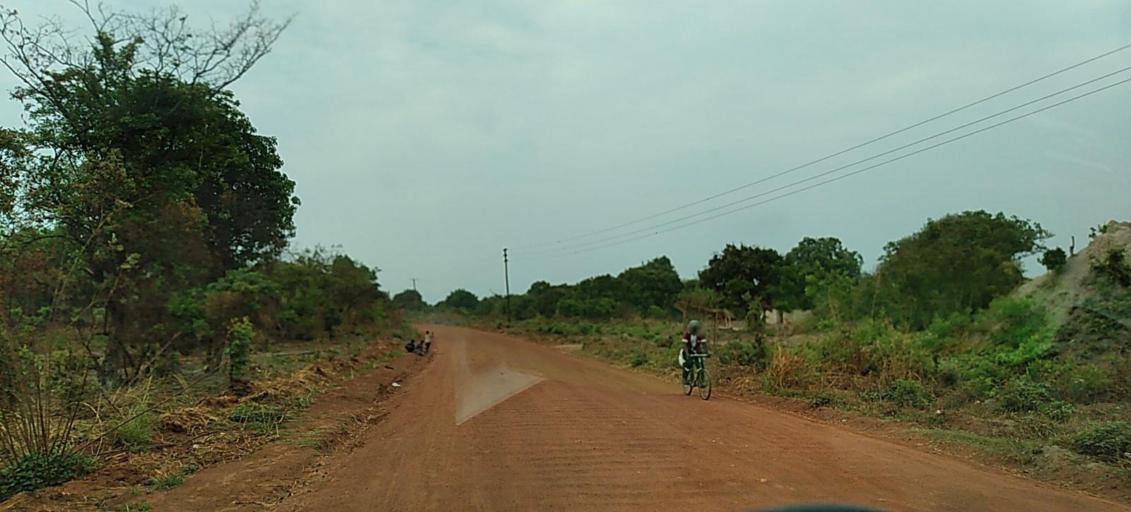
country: ZM
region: North-Western
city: Solwezi
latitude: -12.2366
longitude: 26.5111
